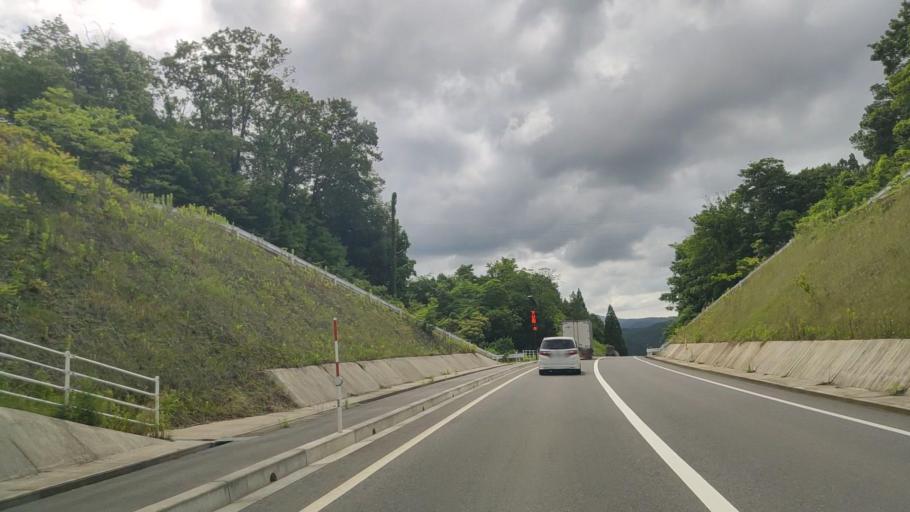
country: JP
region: Tottori
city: Yonago
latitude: 35.3762
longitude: 133.4060
